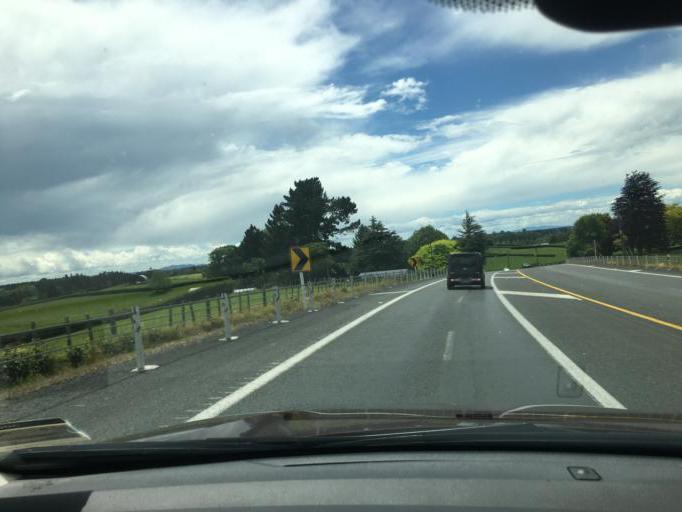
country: NZ
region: Waikato
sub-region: Waipa District
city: Cambridge
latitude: -37.9370
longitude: 175.3144
